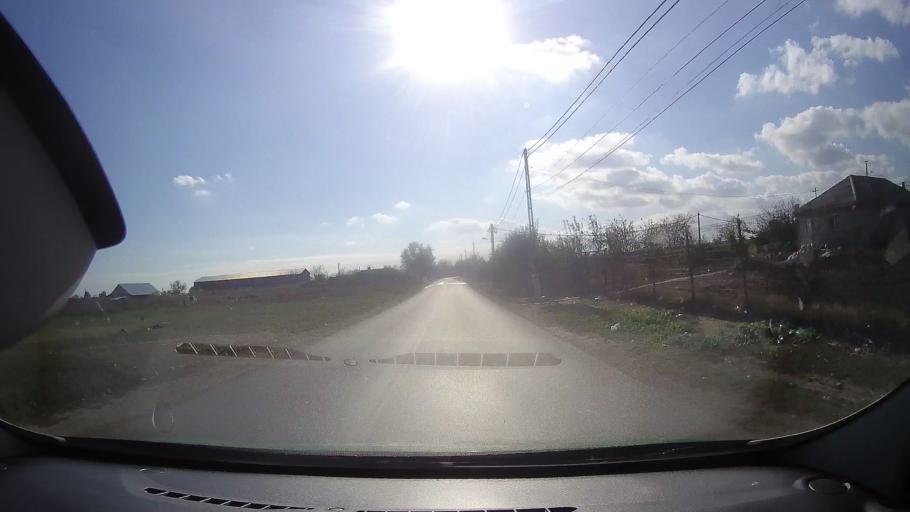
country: RO
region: Constanta
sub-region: Comuna Mihai Viteazu
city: Mihai Viteazu
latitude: 44.6284
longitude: 28.7321
